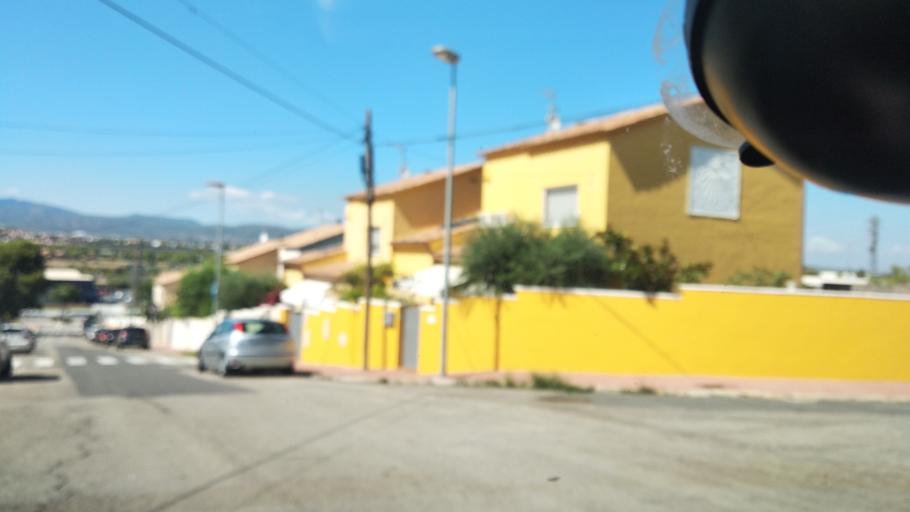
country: ES
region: Catalonia
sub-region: Provincia de Tarragona
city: El Vendrell
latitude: 41.2229
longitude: 1.5443
